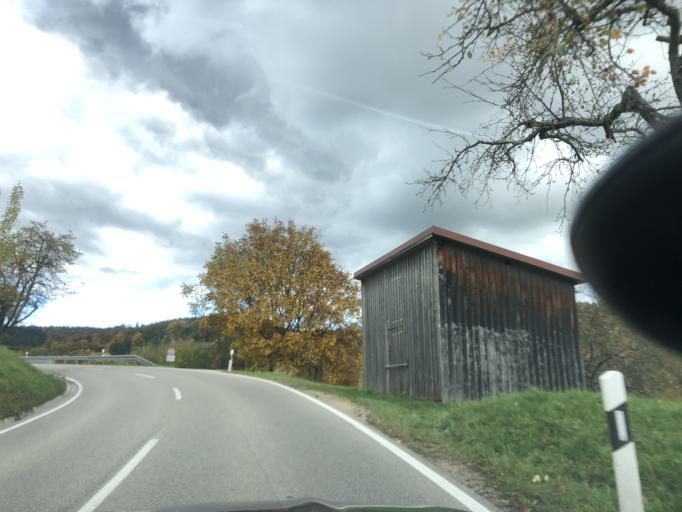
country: DE
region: Baden-Wuerttemberg
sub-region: Regierungsbezirk Stuttgart
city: Winterbach
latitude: 48.8120
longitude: 9.4701
